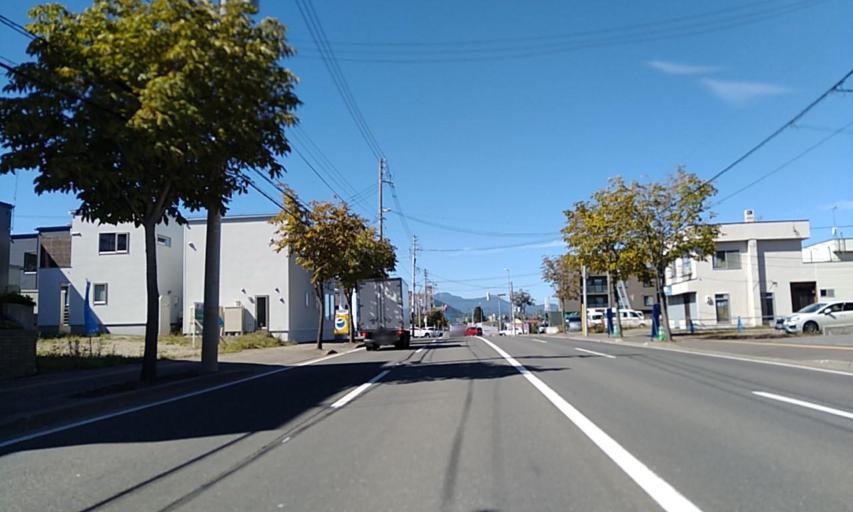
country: JP
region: Hokkaido
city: Sapporo
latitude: 43.0042
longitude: 141.3901
